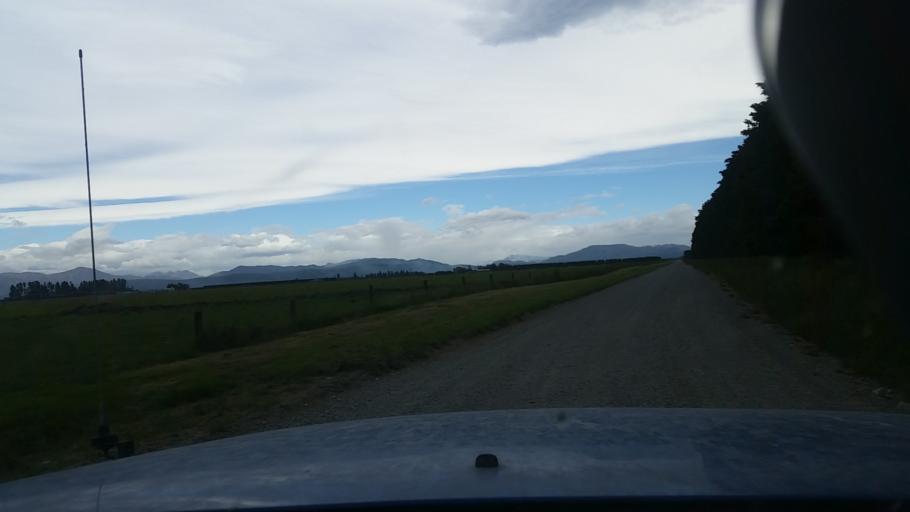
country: NZ
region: Canterbury
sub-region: Ashburton District
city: Methven
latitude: -43.7937
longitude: 171.5136
